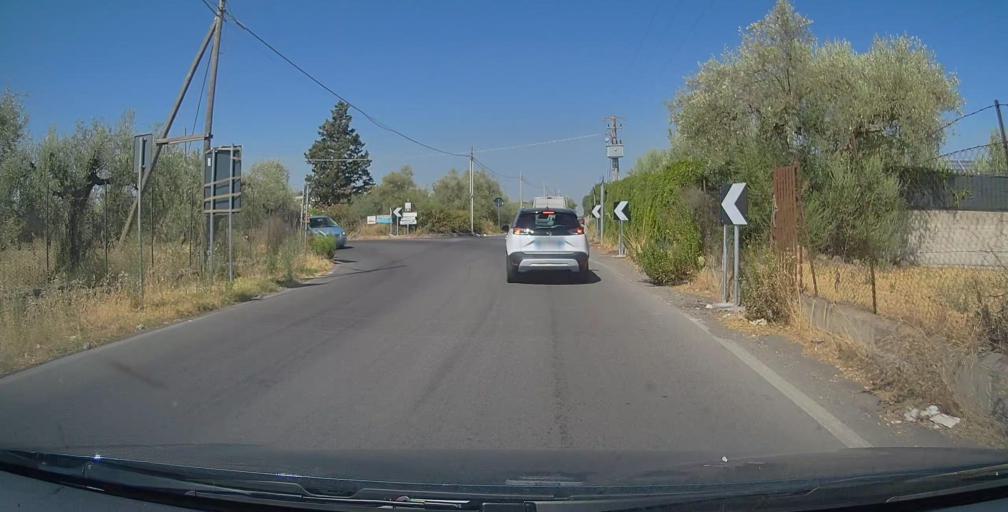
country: IT
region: Sicily
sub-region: Catania
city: Palazzolo
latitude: 37.5465
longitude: 14.9308
